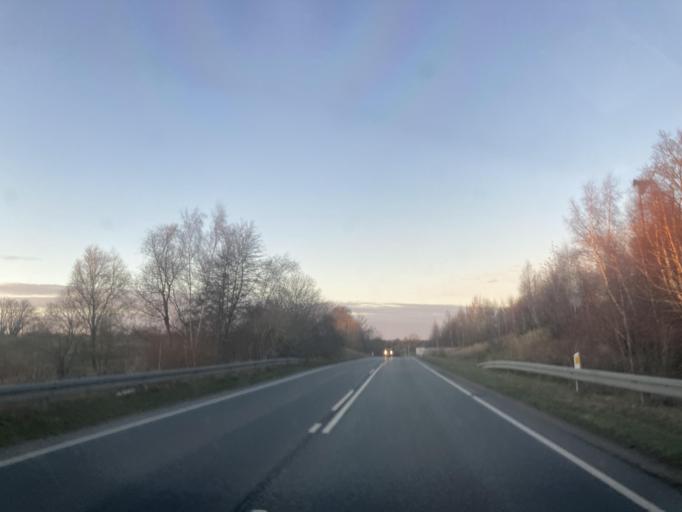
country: DK
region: Capital Region
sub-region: Gribskov Kommune
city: Graested
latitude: 56.0566
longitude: 12.2755
